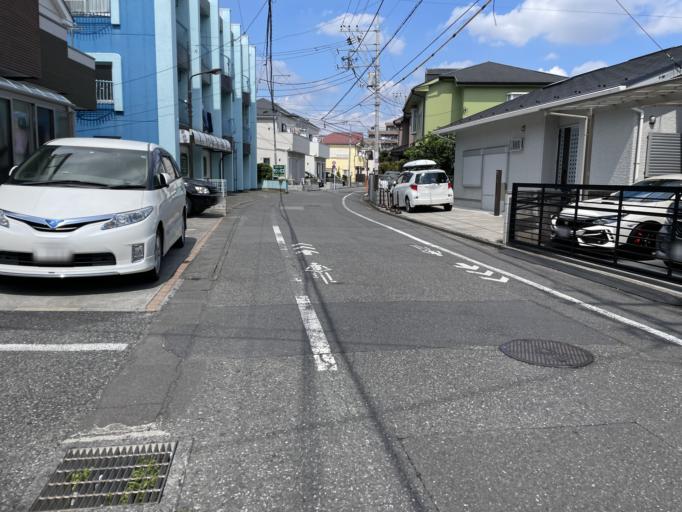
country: JP
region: Tokyo
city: Fussa
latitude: 35.7445
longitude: 139.3292
